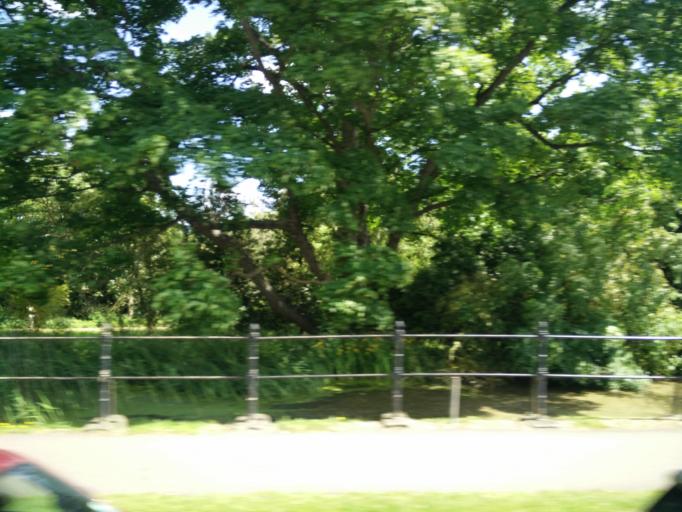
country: GB
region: England
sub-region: Cambridgeshire
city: Cambridge
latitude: 52.1939
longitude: 0.1231
